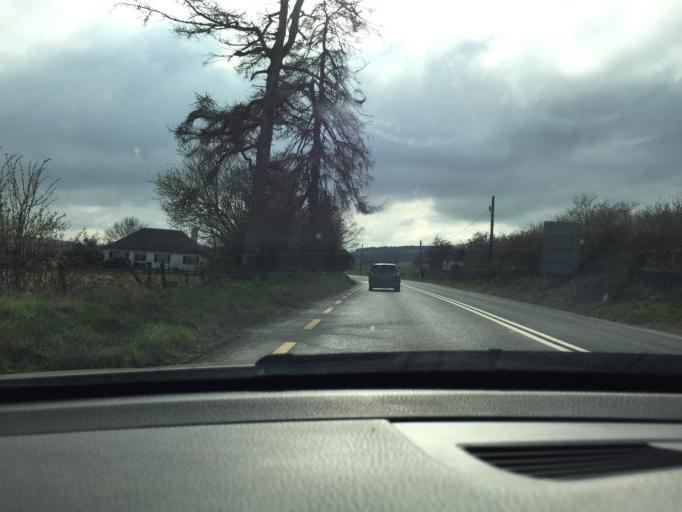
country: IE
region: Leinster
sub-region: South Dublin
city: Saggart
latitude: 53.2315
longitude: -6.4580
